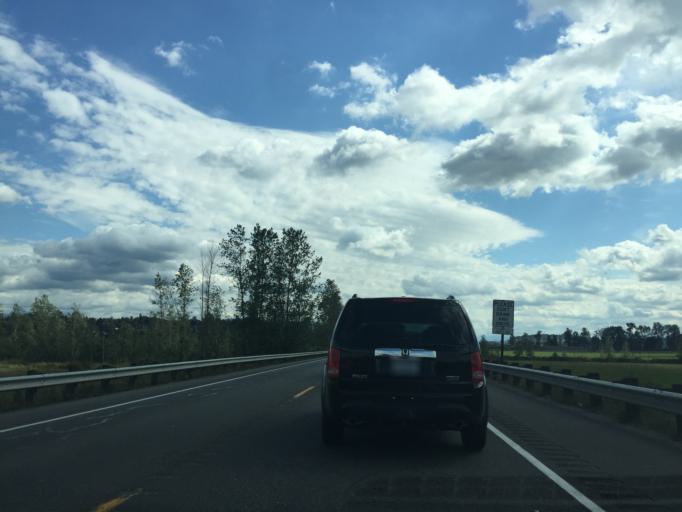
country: US
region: Washington
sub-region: Snohomish County
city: Three Lakes
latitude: 47.8890
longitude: -122.0269
